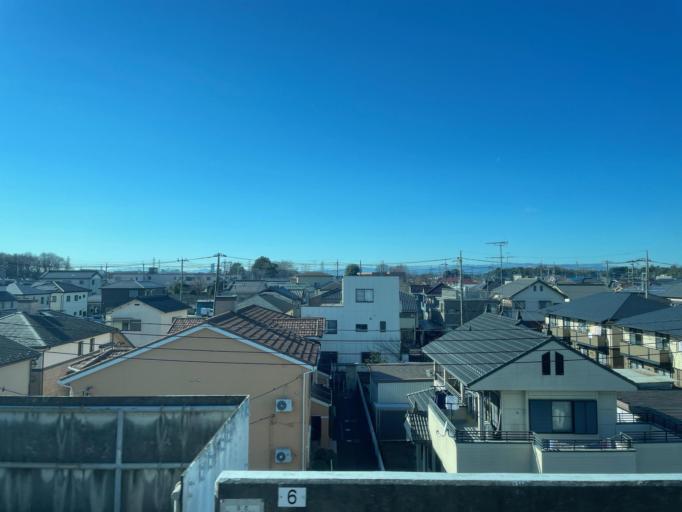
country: JP
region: Saitama
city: Ageoshimo
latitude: 35.9987
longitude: 139.6178
